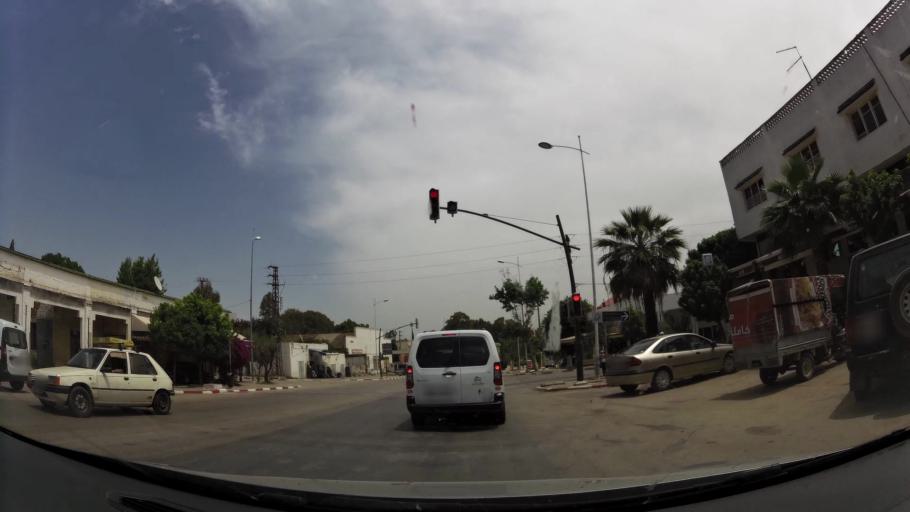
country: MA
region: Rabat-Sale-Zemmour-Zaer
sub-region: Khemisset
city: Khemisset
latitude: 33.8245
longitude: -6.0644
